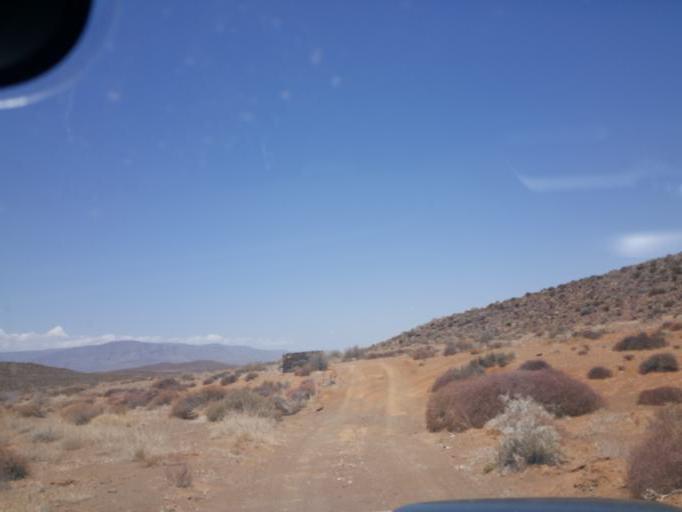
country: ZA
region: Northern Cape
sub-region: Namakwa District Municipality
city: Calvinia
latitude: -32.1994
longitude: 20.0053
